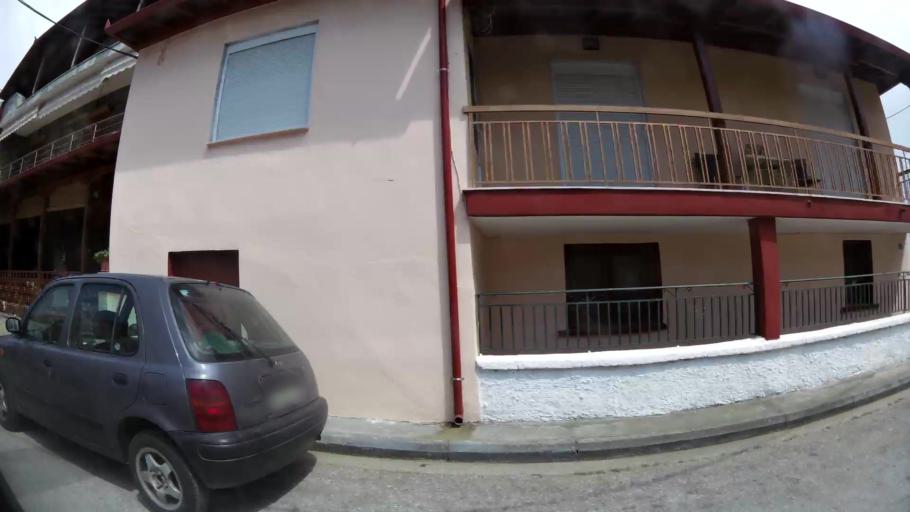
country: GR
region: Central Macedonia
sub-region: Nomos Pierias
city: Korinos
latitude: 40.3132
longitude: 22.5766
